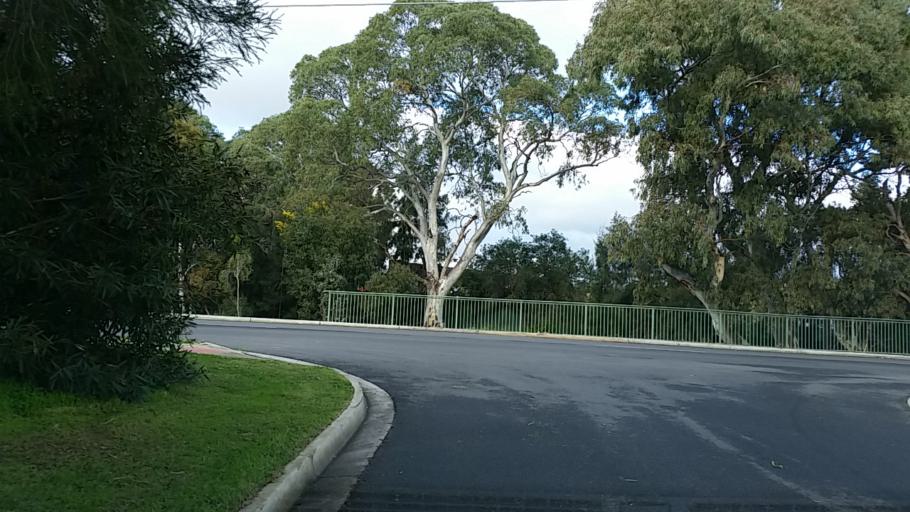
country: AU
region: South Australia
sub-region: Tea Tree Gully
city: Modbury
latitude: -34.8381
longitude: 138.6754
